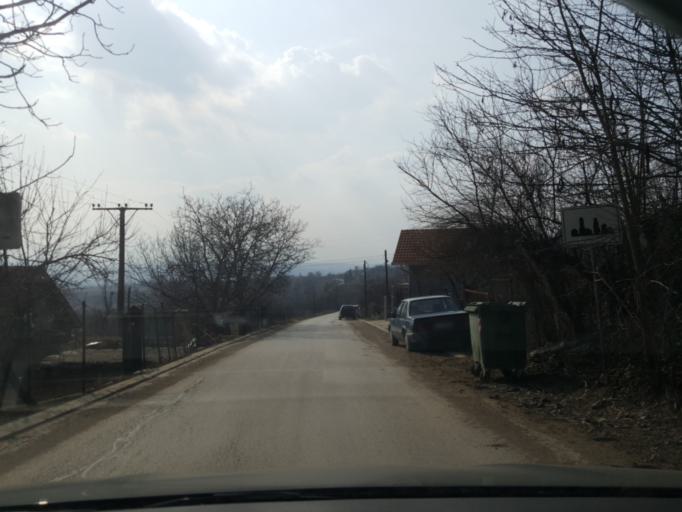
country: RS
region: Central Serbia
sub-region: Nisavski Okrug
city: Aleksinac
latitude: 43.5408
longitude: 21.7340
